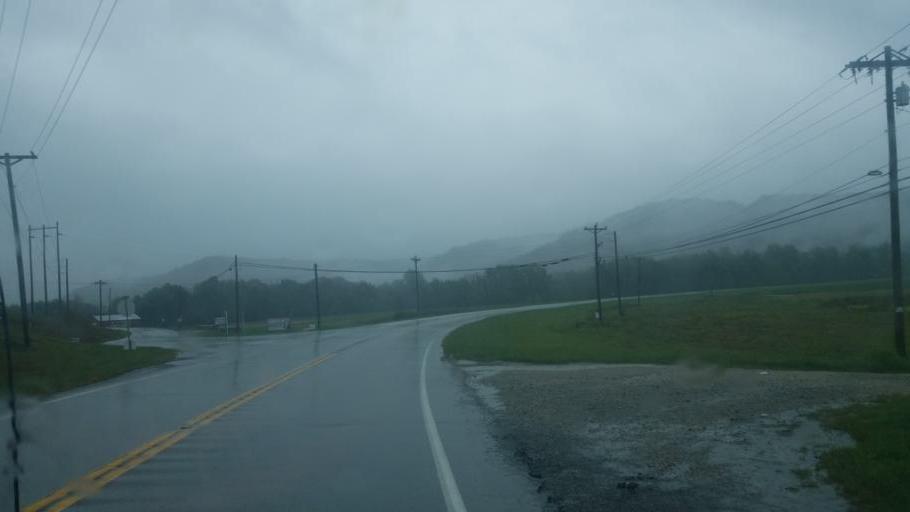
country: US
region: Kentucky
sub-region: Rowan County
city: Morehead
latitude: 38.3157
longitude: -83.5705
